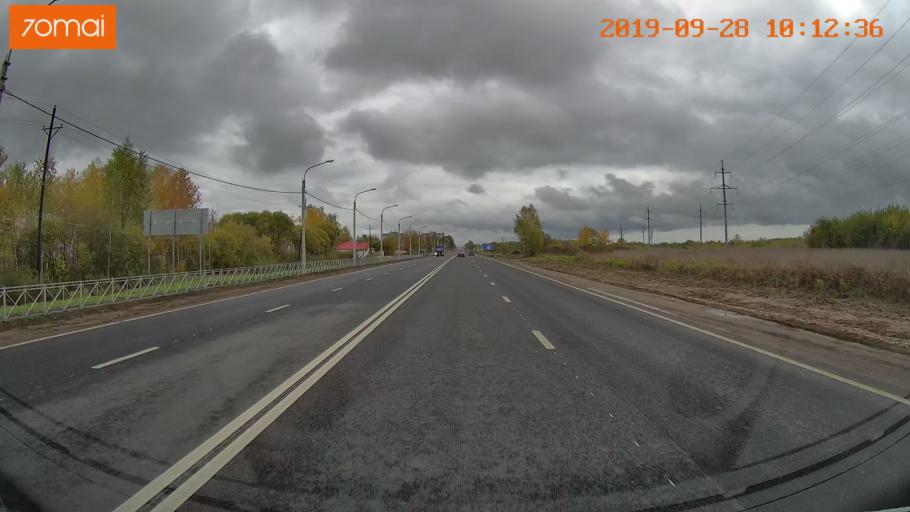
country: RU
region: Jaroslavl
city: Yaroslavl
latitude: 57.5420
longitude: 39.9616
